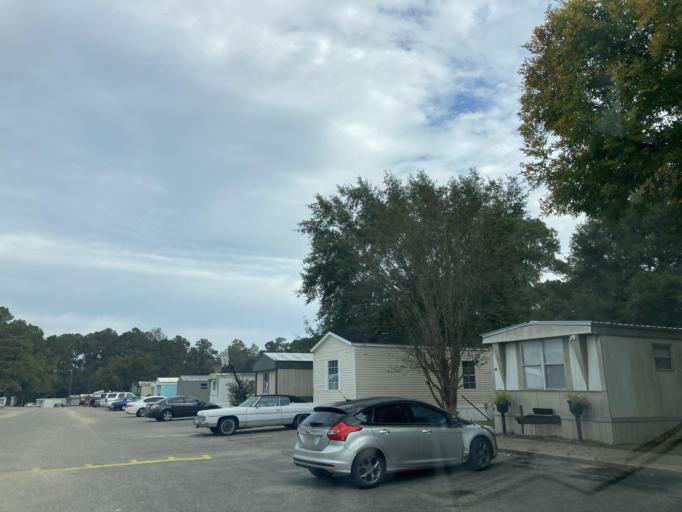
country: US
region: Mississippi
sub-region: Lamar County
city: West Hattiesburg
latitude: 31.3056
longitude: -89.3783
